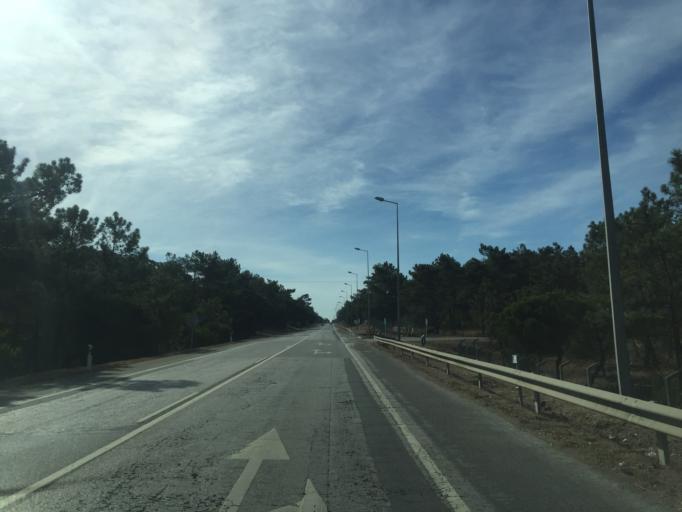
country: PT
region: Coimbra
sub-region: Figueira da Foz
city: Lavos
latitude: 40.1087
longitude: -8.8556
